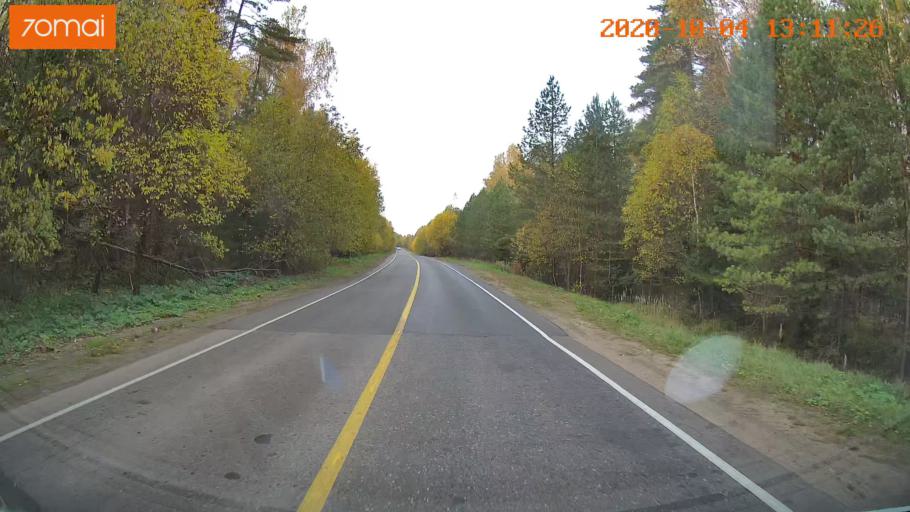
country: RU
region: Ivanovo
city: Bogorodskoye
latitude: 57.0771
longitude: 40.9450
